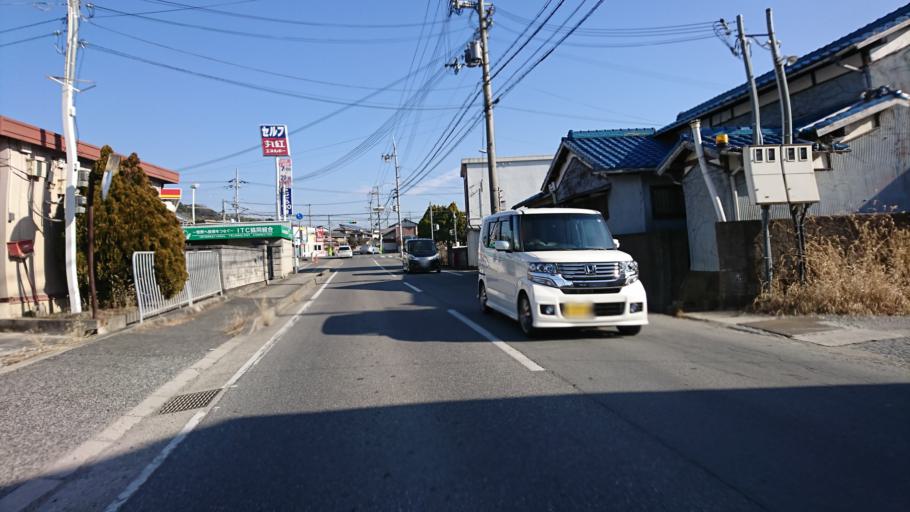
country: JP
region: Hyogo
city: Kakogawacho-honmachi
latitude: 34.8146
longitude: 134.8349
